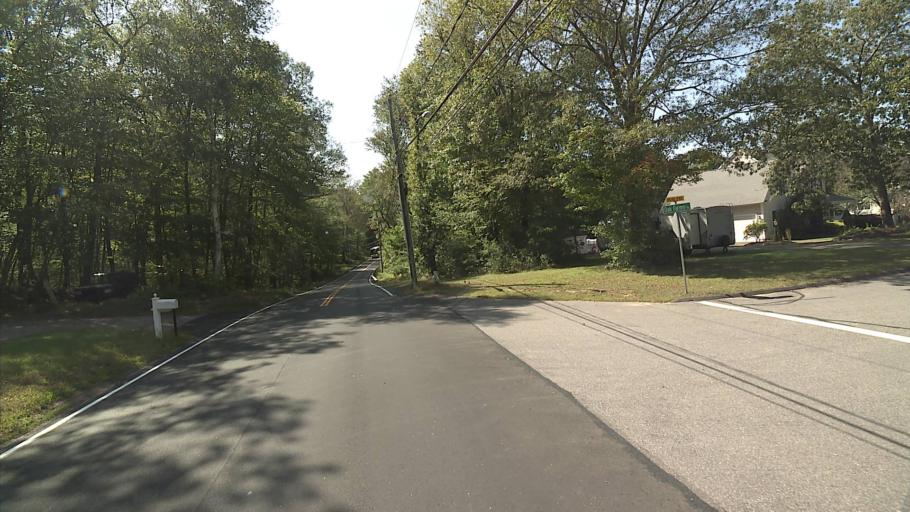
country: US
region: Connecticut
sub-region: Tolland County
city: Hebron
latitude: 41.7238
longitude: -72.4047
